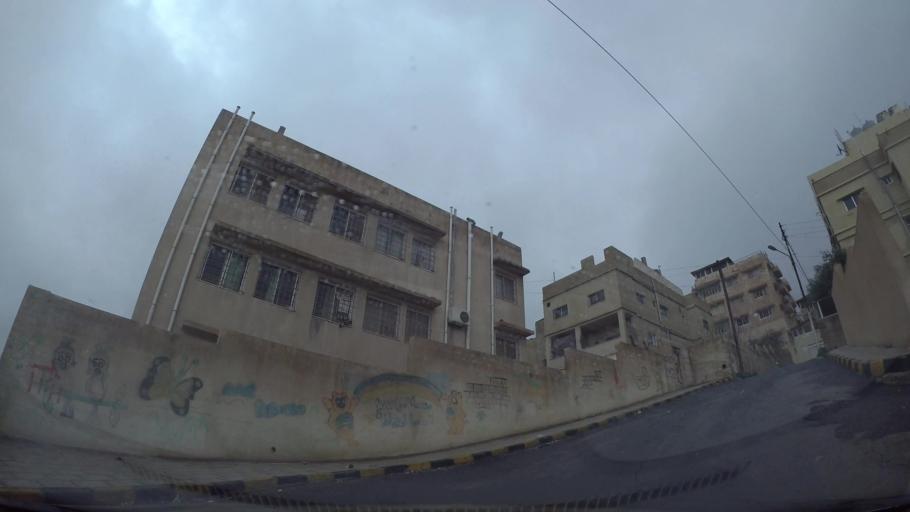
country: JO
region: Amman
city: Amman
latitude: 31.9481
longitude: 35.9110
